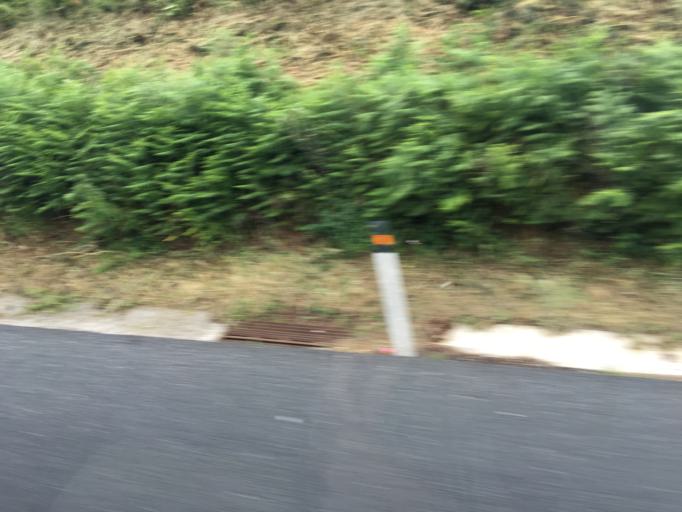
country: IT
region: Latium
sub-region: Citta metropolitana di Roma Capitale
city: Valmontone
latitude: 41.7660
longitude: 12.9249
